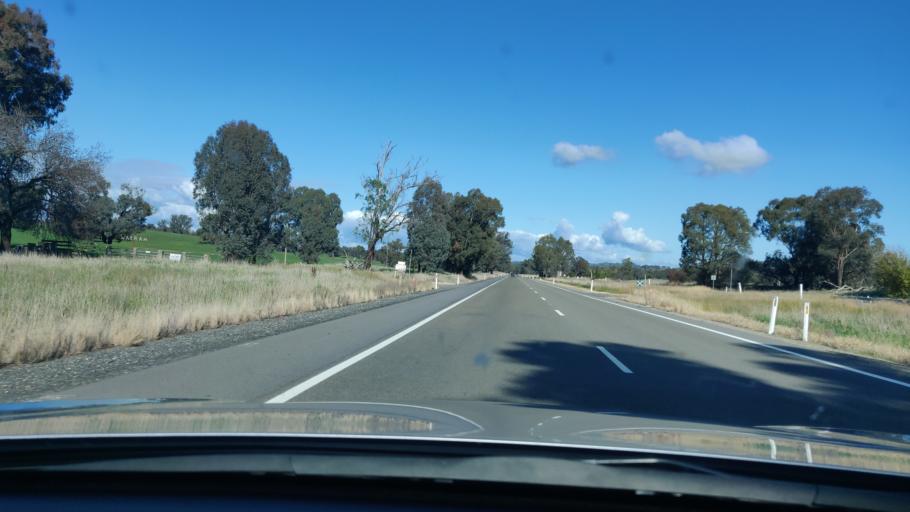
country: AU
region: New South Wales
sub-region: Greater Hume Shire
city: Holbrook
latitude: -35.5303
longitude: 147.5476
